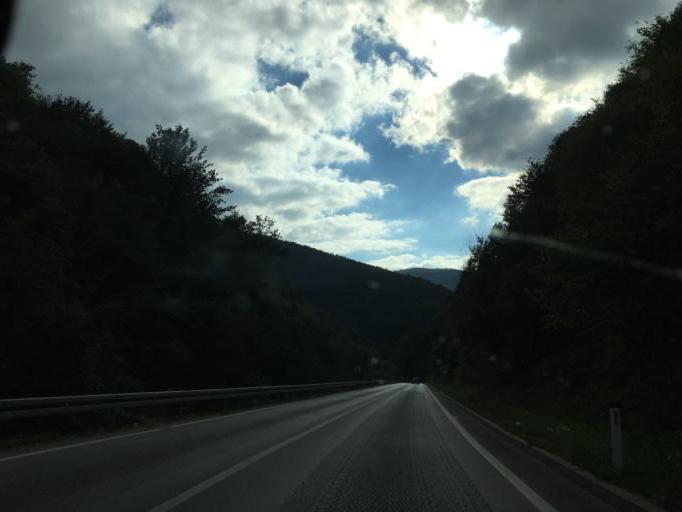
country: BA
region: Federation of Bosnia and Herzegovina
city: Novi Travnik
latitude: 44.0952
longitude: 17.5753
